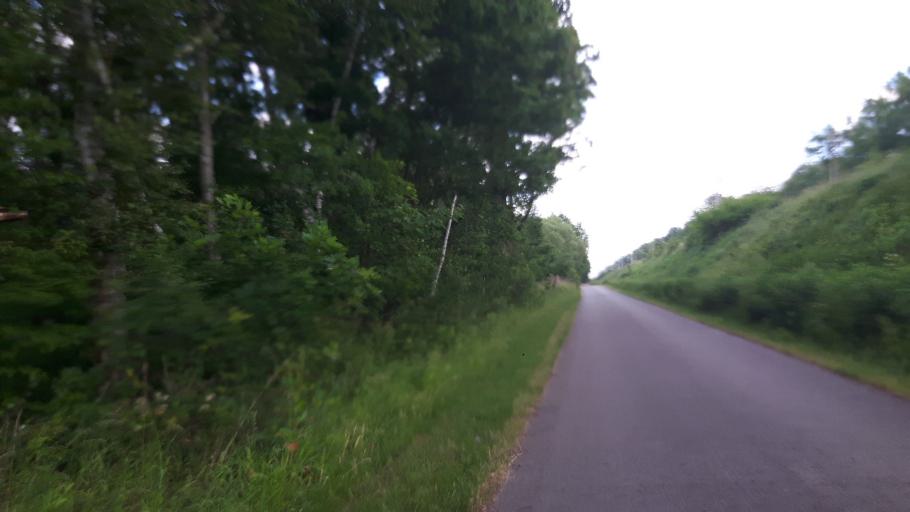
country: DE
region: Saxony-Anhalt
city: Bergwitz
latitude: 51.7893
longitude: 12.5547
